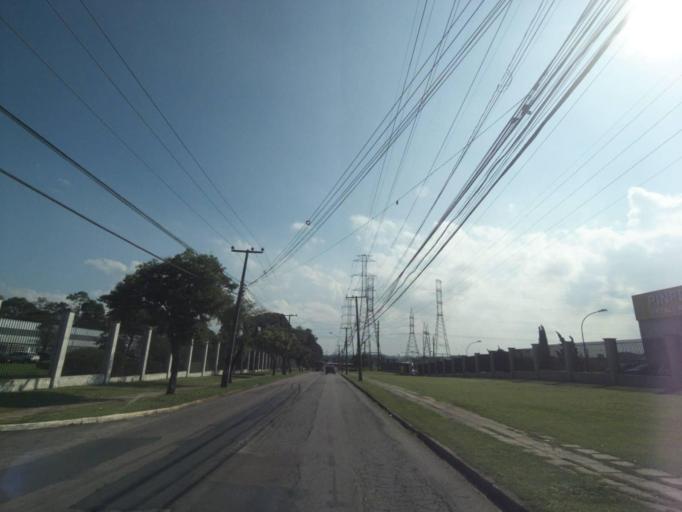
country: BR
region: Parana
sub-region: Araucaria
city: Araucaria
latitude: -25.5321
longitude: -49.3294
